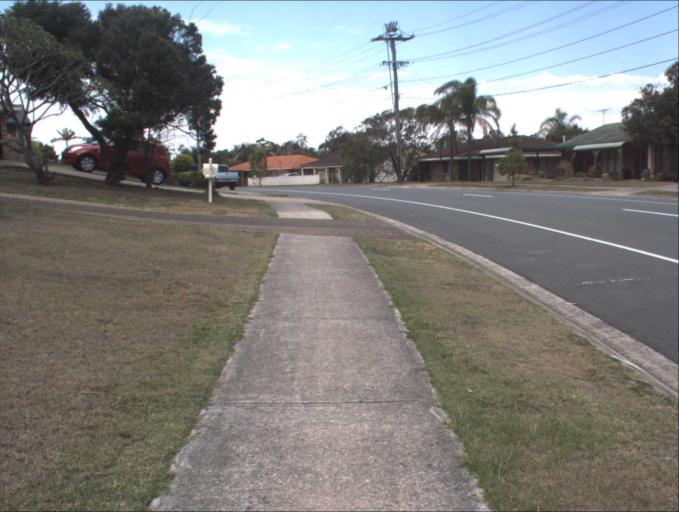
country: AU
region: Queensland
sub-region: Logan
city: Slacks Creek
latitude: -27.6376
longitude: 153.1420
